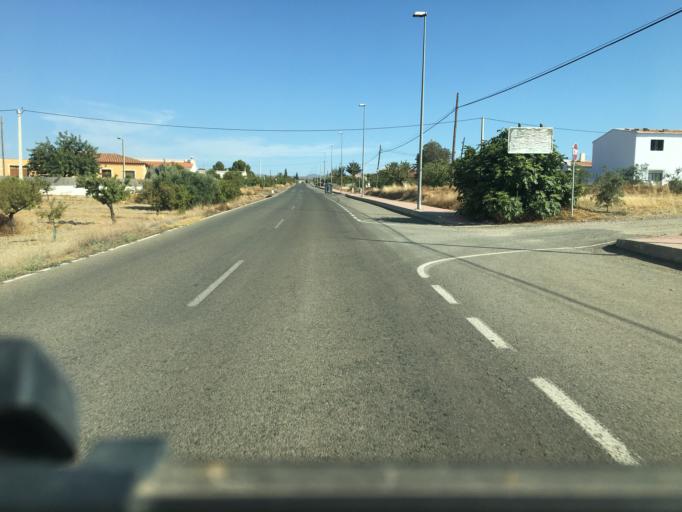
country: ES
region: Andalusia
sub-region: Provincia de Almeria
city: Huercal-Overa
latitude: 37.4466
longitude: -1.9827
